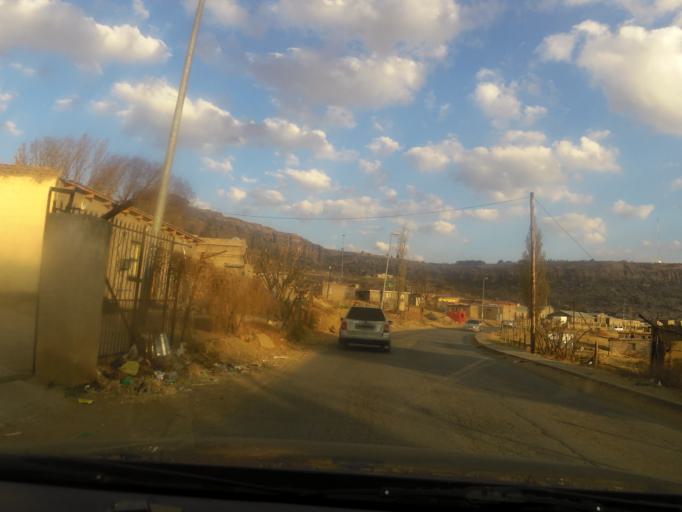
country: LS
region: Maseru
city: Maseru
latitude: -29.3118
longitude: 27.5381
